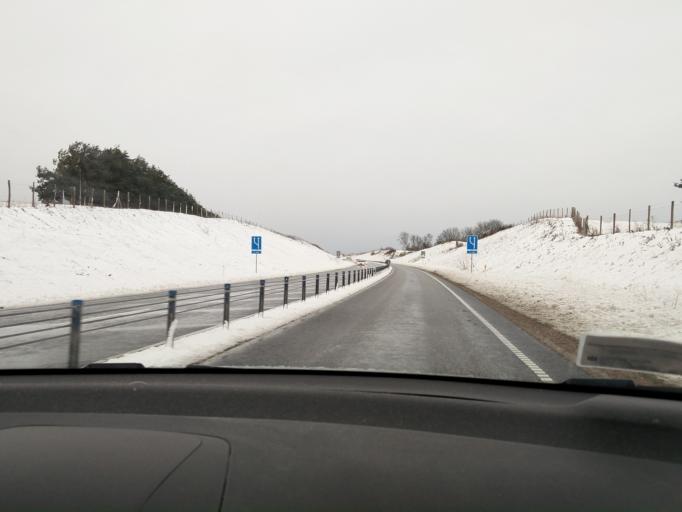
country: DK
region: Zealand
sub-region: Odsherred Kommune
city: Hojby
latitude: 55.8273
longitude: 11.5884
